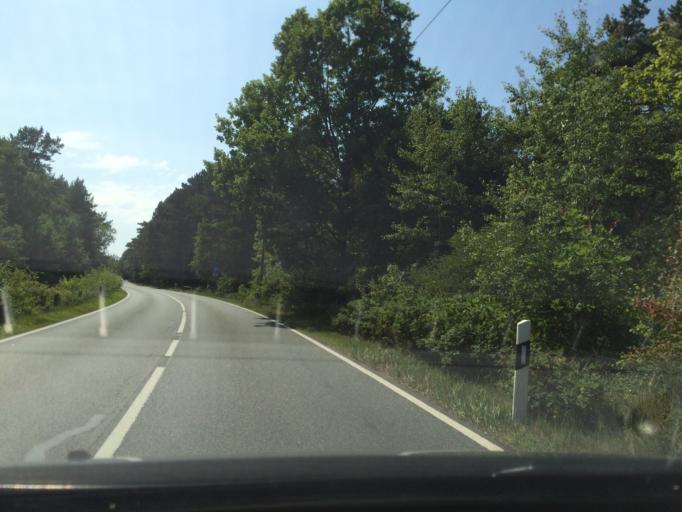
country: DE
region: Mecklenburg-Vorpommern
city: Ostseebad Prerow
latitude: 54.4501
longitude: 12.5935
